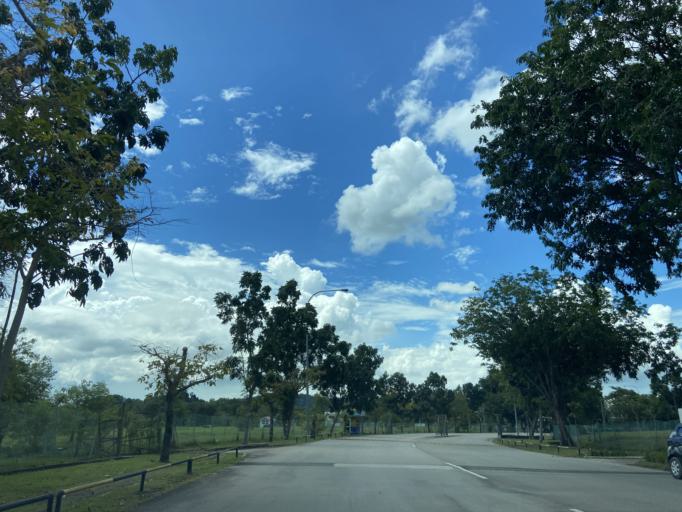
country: SG
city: Singapore
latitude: 1.0589
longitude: 104.0293
